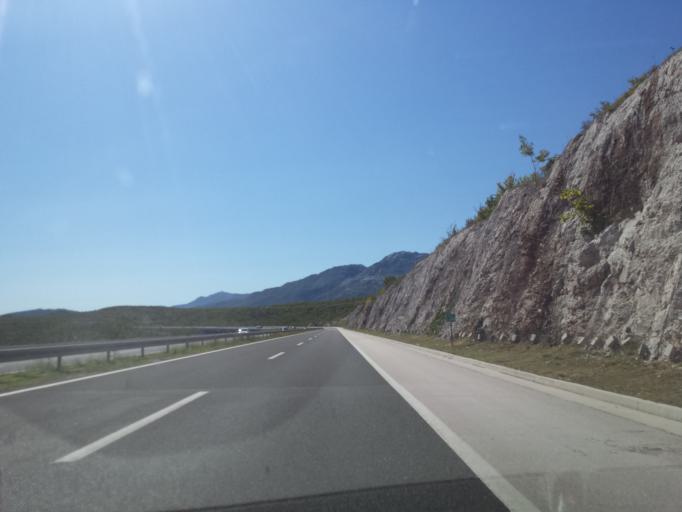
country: HR
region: Splitsko-Dalmatinska
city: Dugopolje
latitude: 43.5960
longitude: 16.6254
